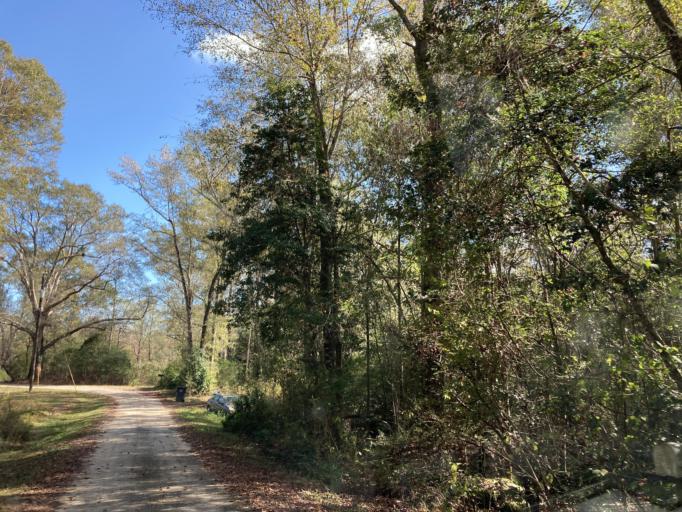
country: US
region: Mississippi
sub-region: Lamar County
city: Purvis
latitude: 31.2369
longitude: -89.4293
